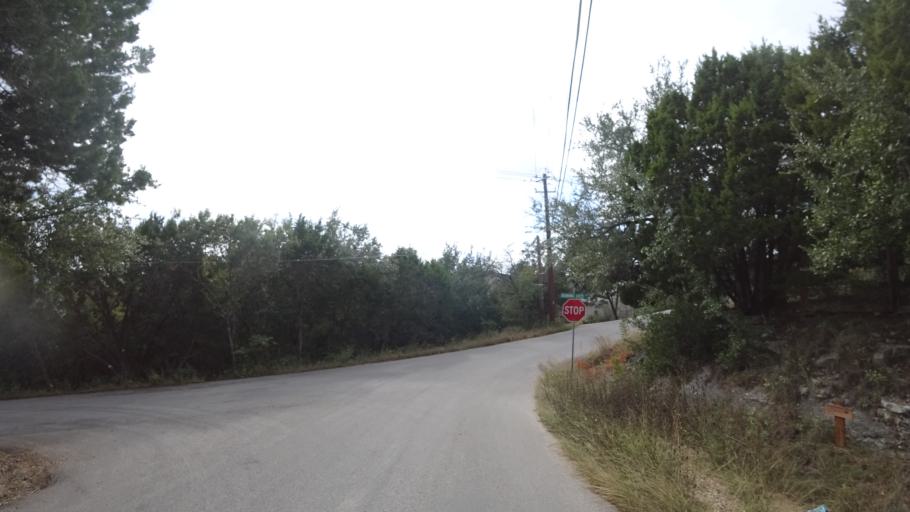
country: US
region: Texas
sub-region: Travis County
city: Hudson Bend
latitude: 30.3735
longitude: -97.9204
